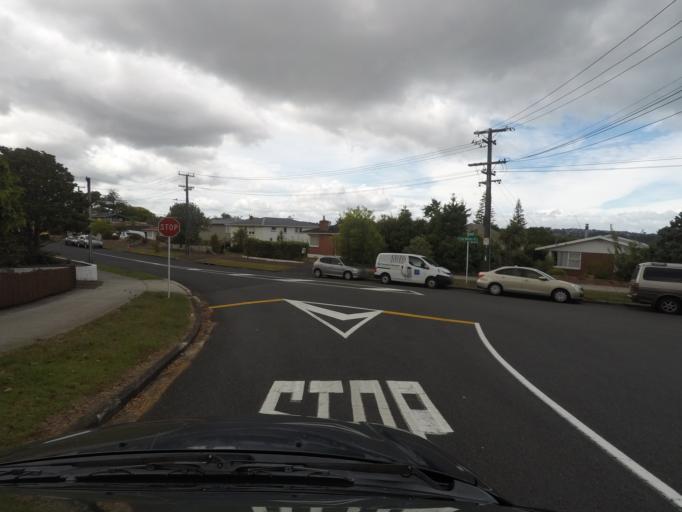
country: NZ
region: Auckland
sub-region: Auckland
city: Rosebank
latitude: -36.9092
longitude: 174.7130
